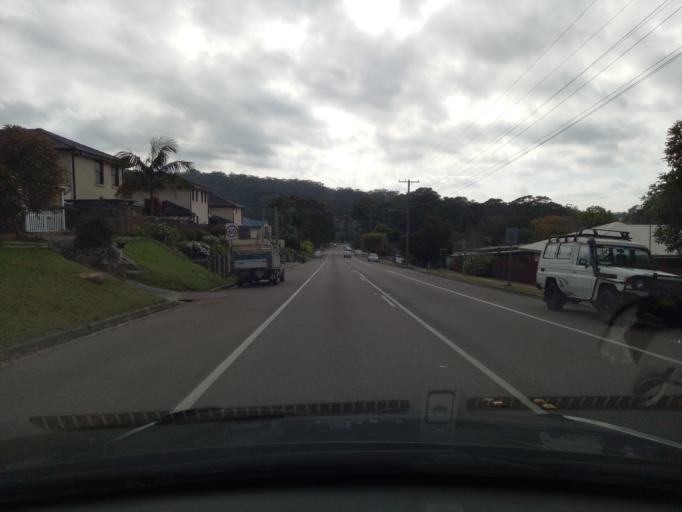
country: AU
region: New South Wales
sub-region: Gosford Shire
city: East Gosford
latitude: -33.4330
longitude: 151.3552
